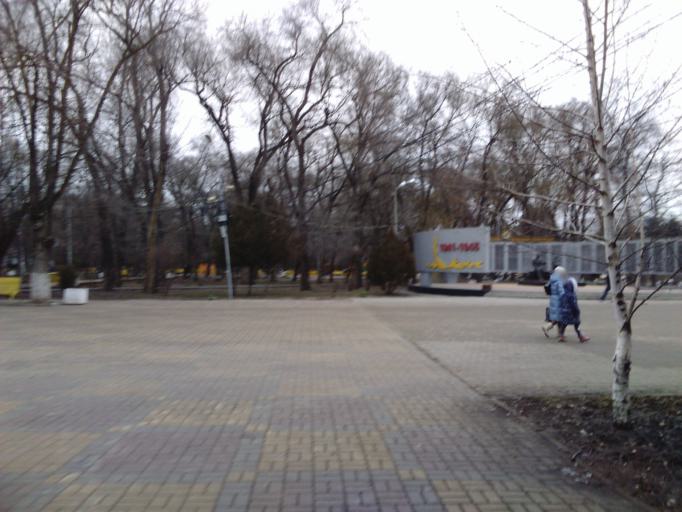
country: RU
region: Rostov
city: Bataysk
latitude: 47.1369
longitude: 39.7439
